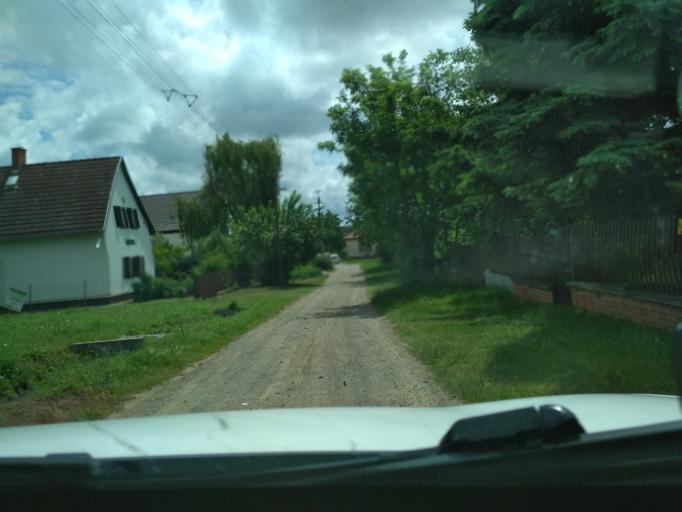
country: HU
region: Jasz-Nagykun-Szolnok
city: Tiszafured
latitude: 47.6106
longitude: 20.7283
